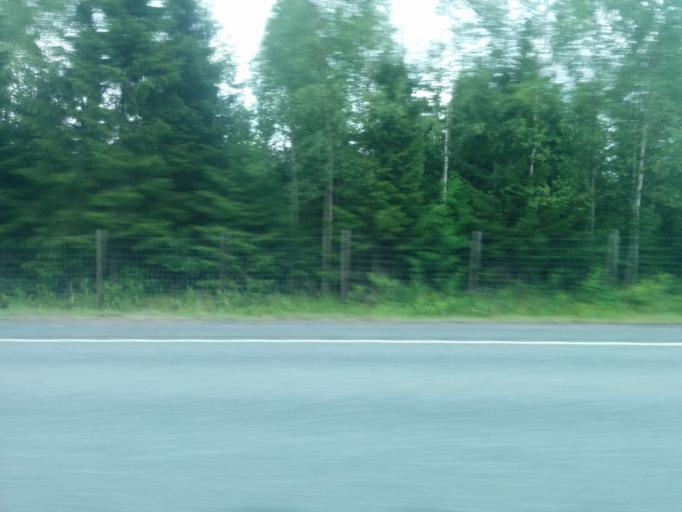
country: FI
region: Pirkanmaa
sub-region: Tampere
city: Orivesi
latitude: 61.6627
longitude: 24.2636
